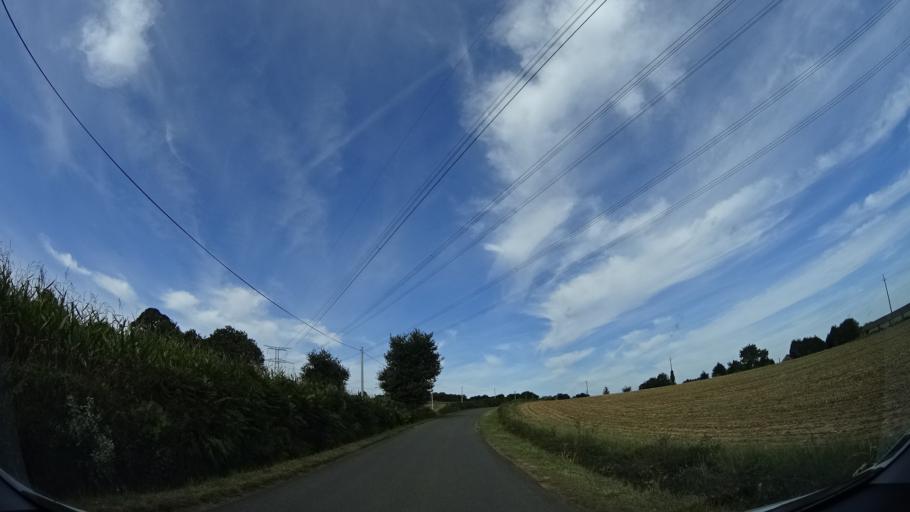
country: FR
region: Brittany
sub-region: Departement d'Ille-et-Vilaine
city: Romagne
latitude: 48.3304
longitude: -1.2614
